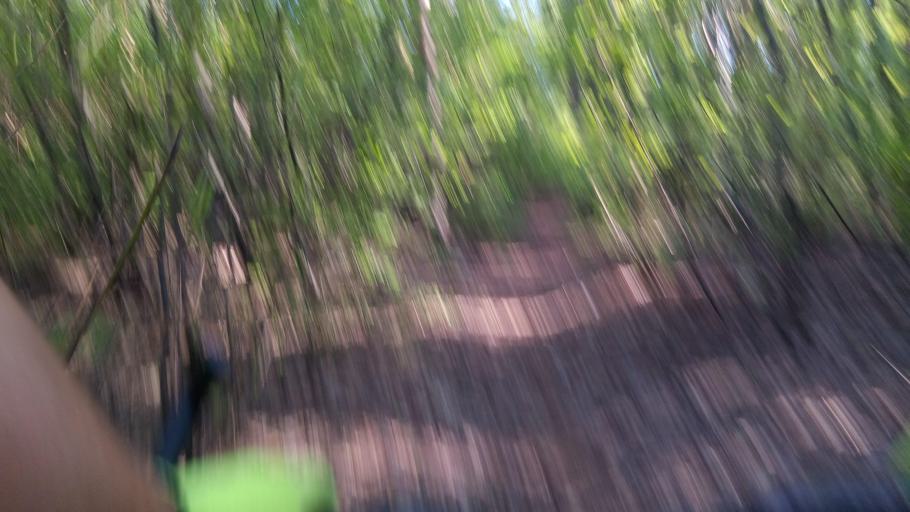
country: RU
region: Chelyabinsk
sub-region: Gorod Chelyabinsk
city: Chelyabinsk
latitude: 55.1485
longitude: 61.3458
